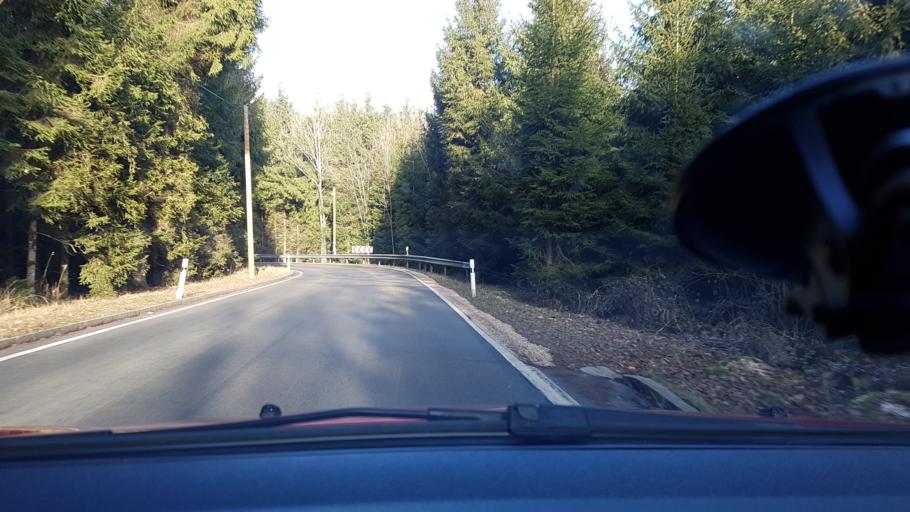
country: DE
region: Bavaria
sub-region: Lower Bavaria
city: Wittibreut
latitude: 48.3323
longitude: 12.9773
